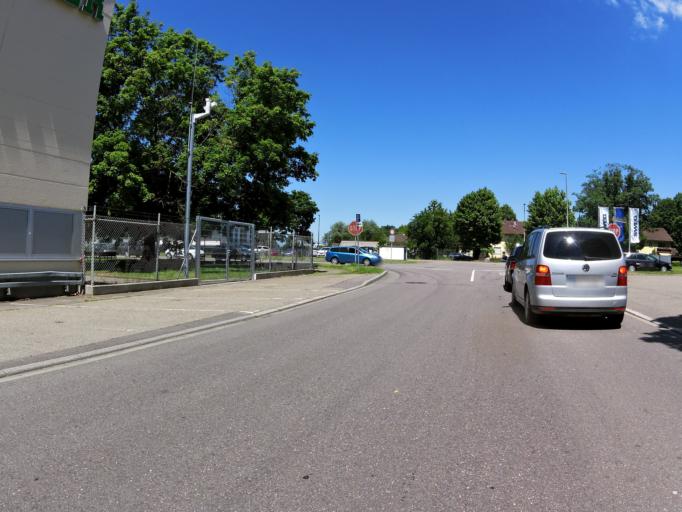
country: DE
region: Baden-Wuerttemberg
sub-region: Freiburg Region
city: Lahr
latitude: 48.3448
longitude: 7.8315
